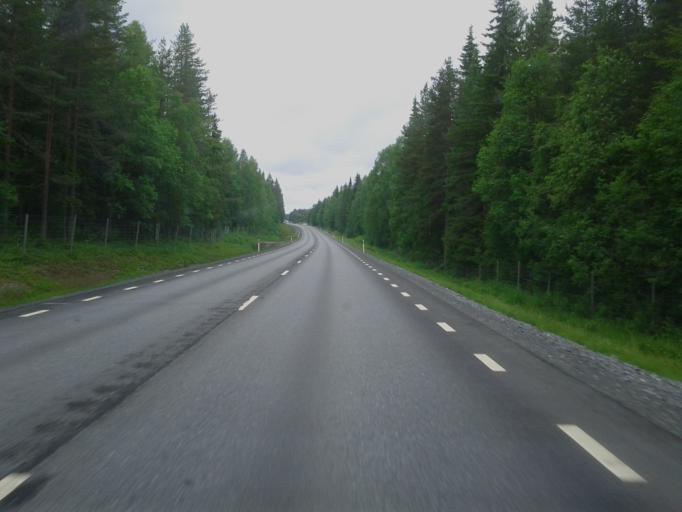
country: SE
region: Vaesterbotten
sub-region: Skelleftea Kommun
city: Forsbacka
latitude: 64.8521
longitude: 20.4847
